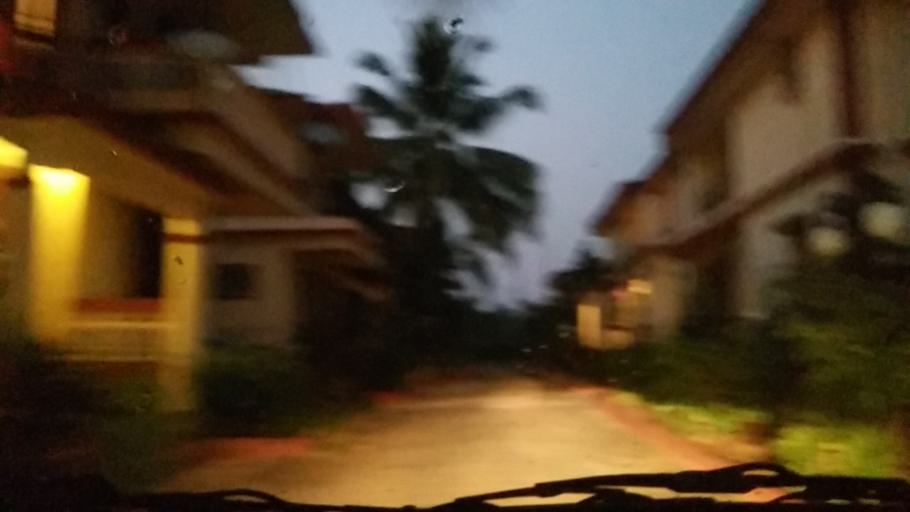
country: IN
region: Goa
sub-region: South Goa
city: Varca
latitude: 15.2059
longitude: 73.9371
